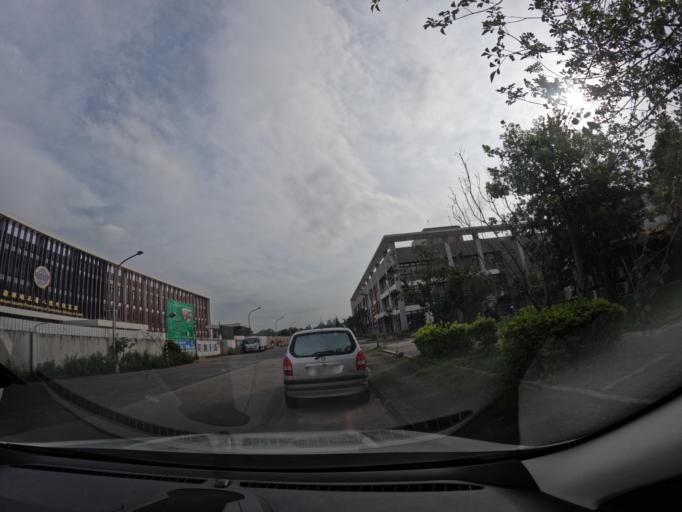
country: TW
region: Taiwan
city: Daxi
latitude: 24.9309
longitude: 121.3034
